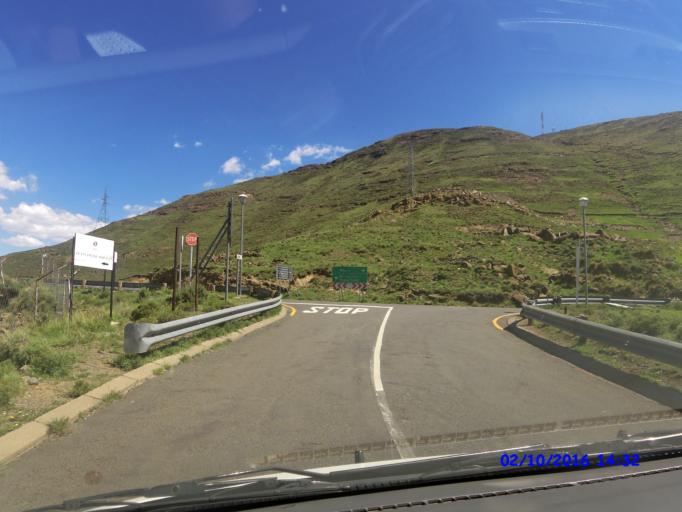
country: LS
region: Maseru
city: Nako
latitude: -29.4820
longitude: 28.0573
